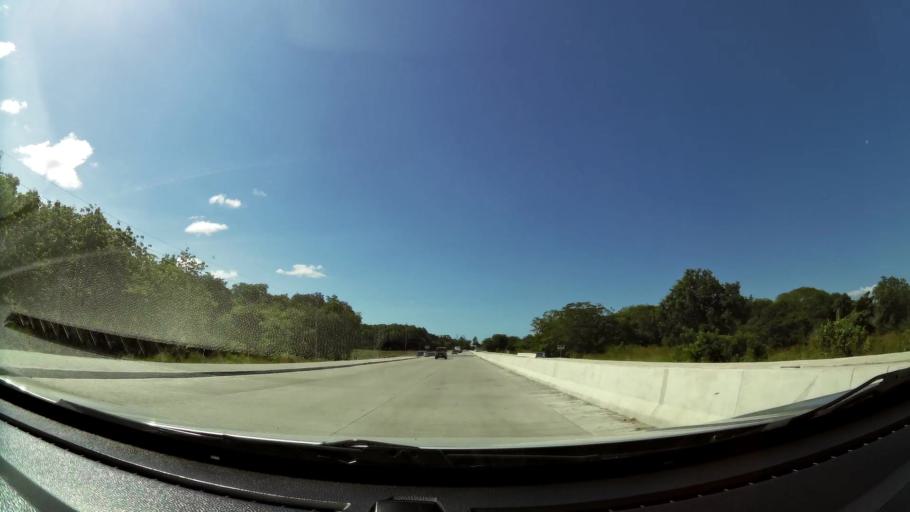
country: CR
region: Guanacaste
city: Bagaces
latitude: 10.5510
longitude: -85.3629
